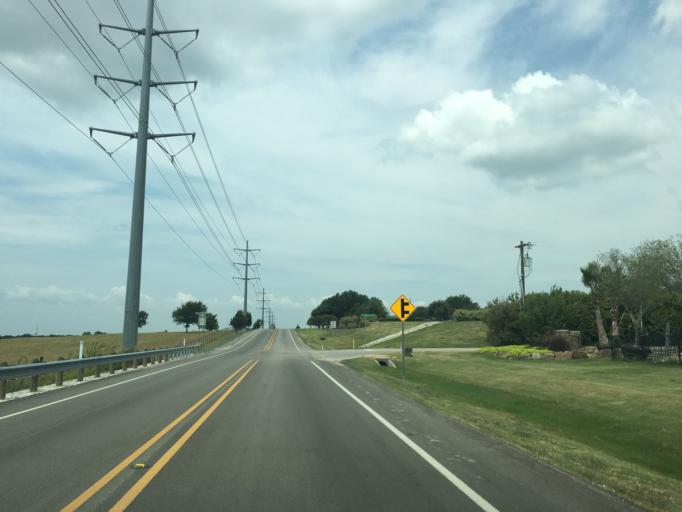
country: US
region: Texas
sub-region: Rockwall County
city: Rockwall
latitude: 32.9364
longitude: -96.4225
